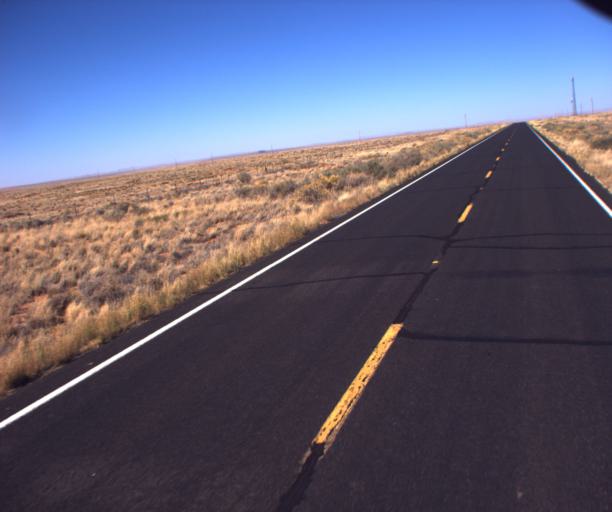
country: US
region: Arizona
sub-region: Navajo County
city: Dilkon
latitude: 35.5083
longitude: -110.4374
